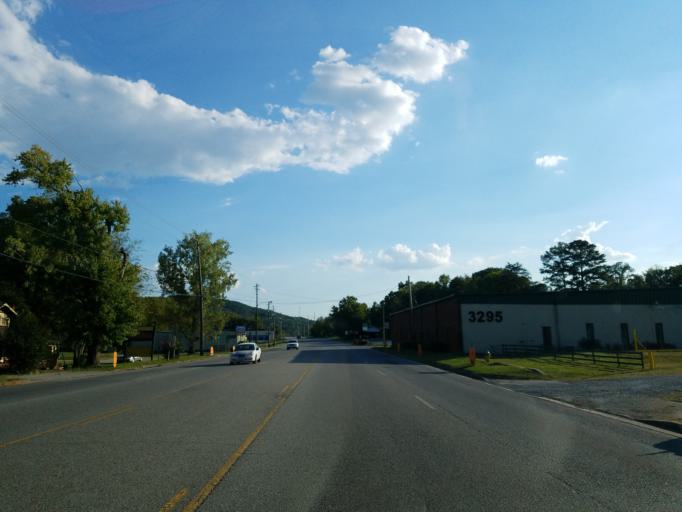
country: US
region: Georgia
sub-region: Murray County
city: Chatsworth
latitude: 34.8233
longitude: -84.7636
